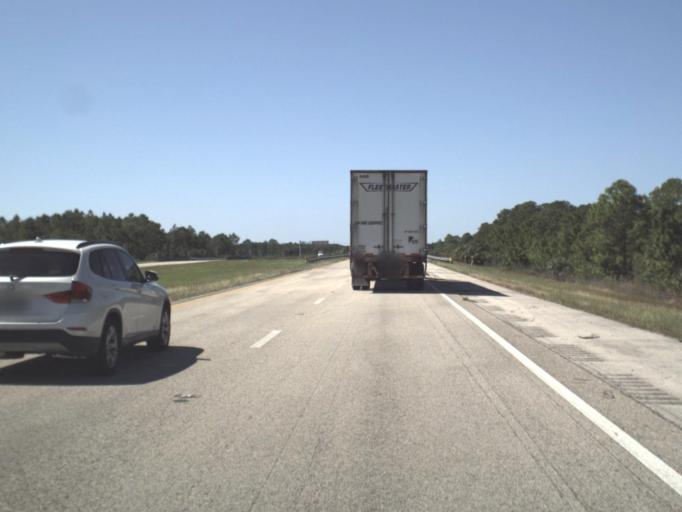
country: US
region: Florida
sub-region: Collier County
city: Orangetree
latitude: 26.1531
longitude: -81.5531
